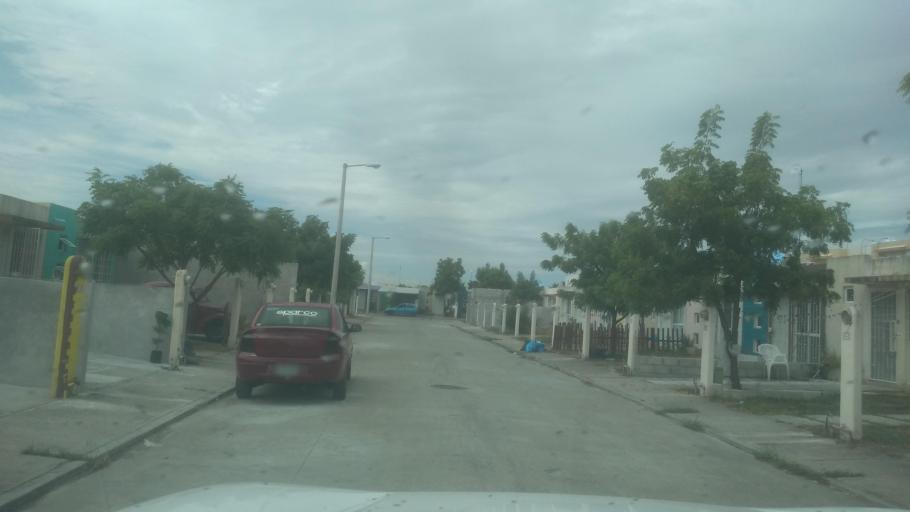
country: MX
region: Veracruz
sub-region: Medellin
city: Fraccionamiento Arboledas San Ramon
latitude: 19.1028
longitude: -96.1680
